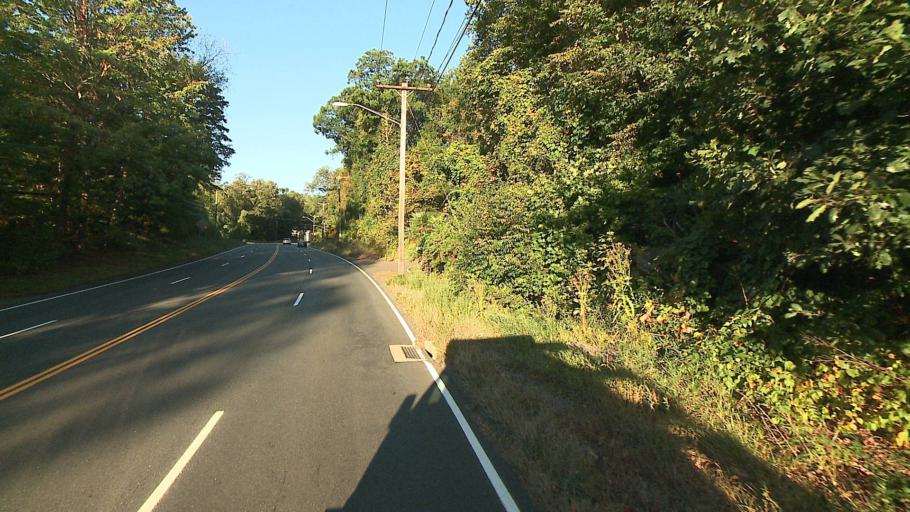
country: US
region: Connecticut
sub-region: Hartford County
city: West Hartford
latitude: 41.7889
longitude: -72.7708
